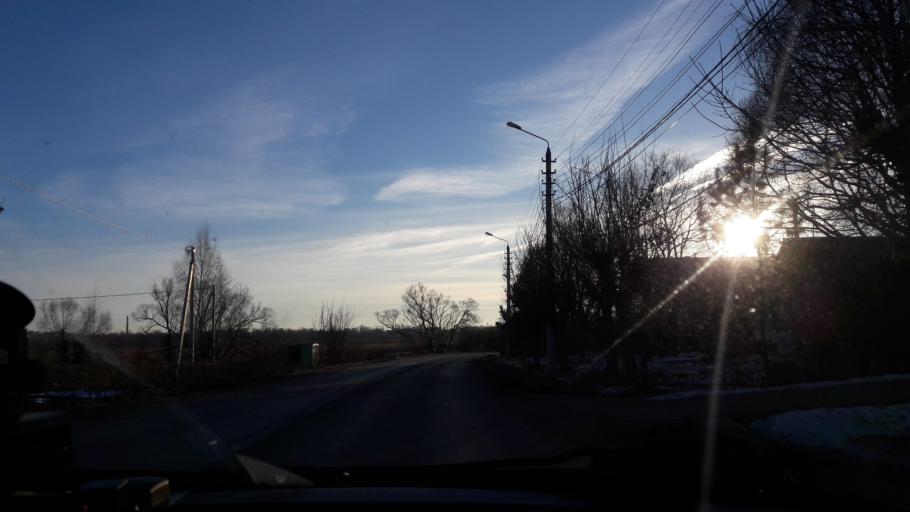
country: RU
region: Tula
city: Gorelki
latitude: 54.2376
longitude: 37.6457
